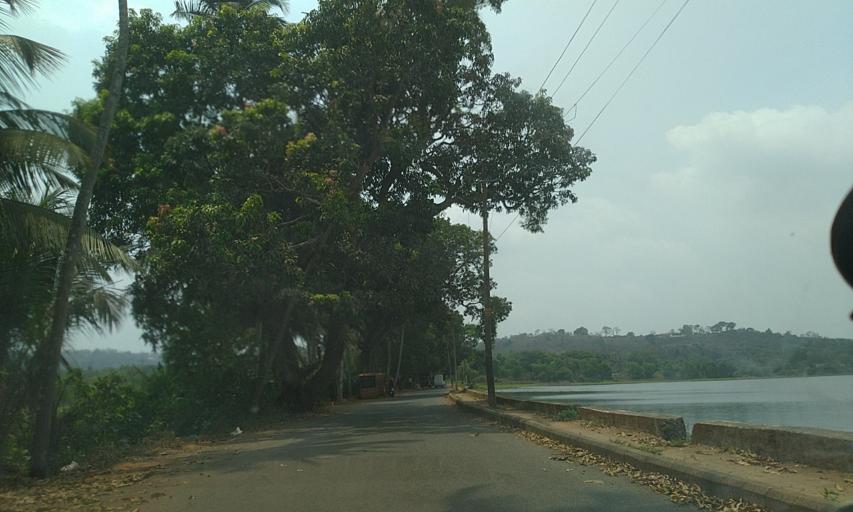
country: IN
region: Goa
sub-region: North Goa
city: Jua
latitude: 15.4862
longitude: 73.9283
